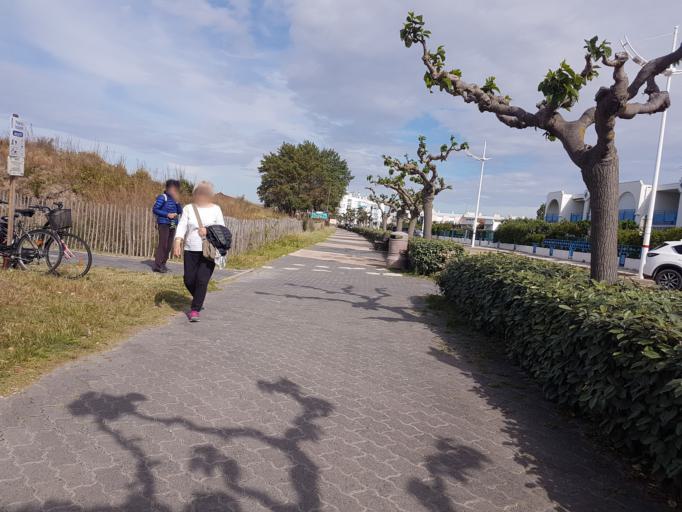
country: FR
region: Languedoc-Roussillon
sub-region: Departement du Gard
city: Le Grau-du-Roi
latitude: 43.5455
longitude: 4.1265
